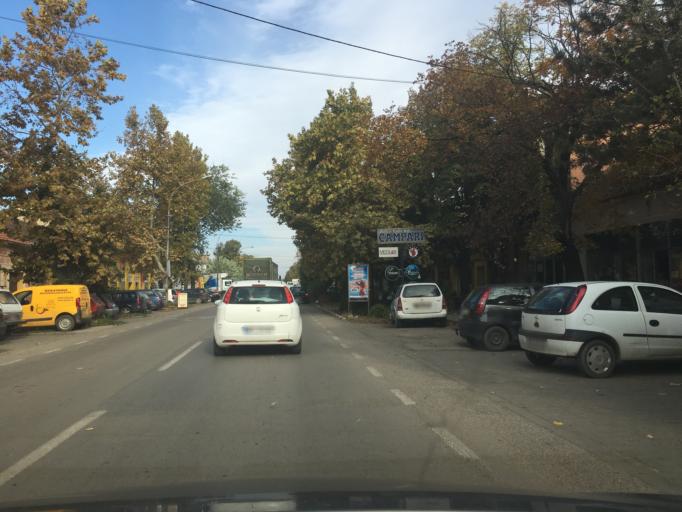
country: RS
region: Autonomna Pokrajina Vojvodina
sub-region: Juznobacki Okrug
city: Zabalj
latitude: 45.3739
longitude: 20.0630
